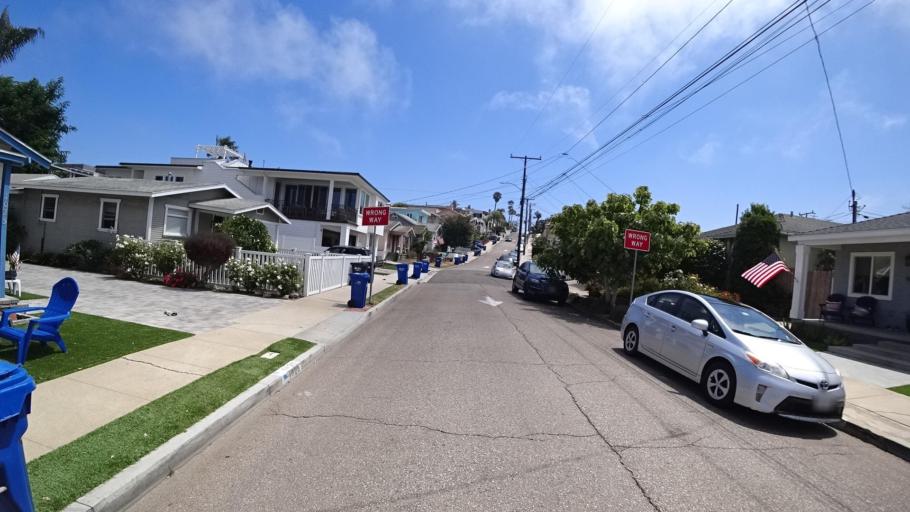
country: US
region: California
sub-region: Los Angeles County
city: Redondo Beach
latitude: 33.8572
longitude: -118.3879
